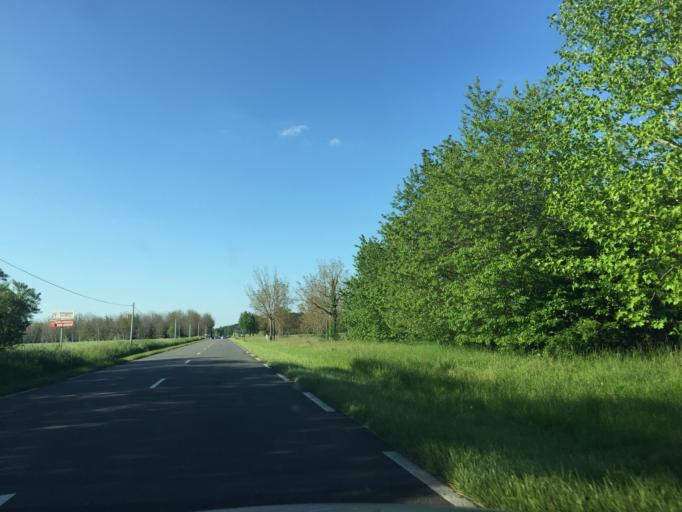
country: FR
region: Poitou-Charentes
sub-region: Departement de la Charente
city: Chalais
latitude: 45.2159
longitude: 0.0332
